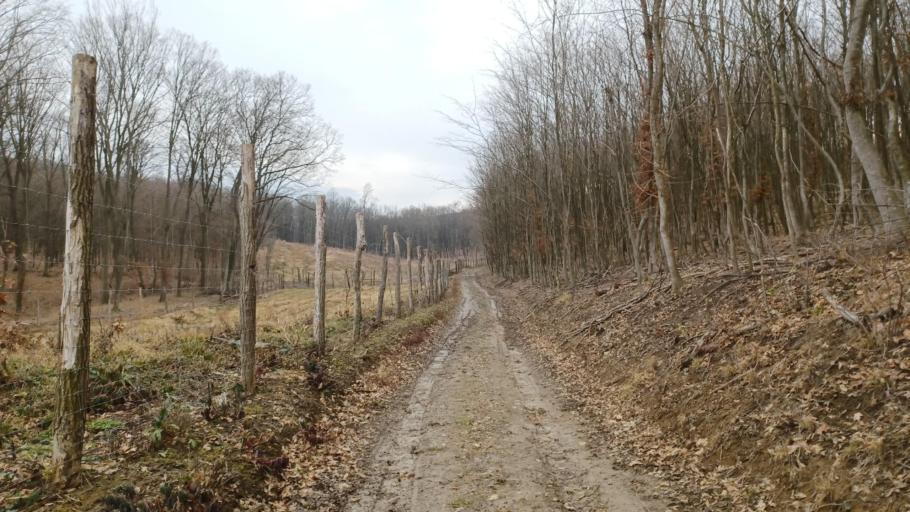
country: HU
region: Tolna
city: Szentgalpuszta
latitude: 46.3105
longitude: 18.6426
